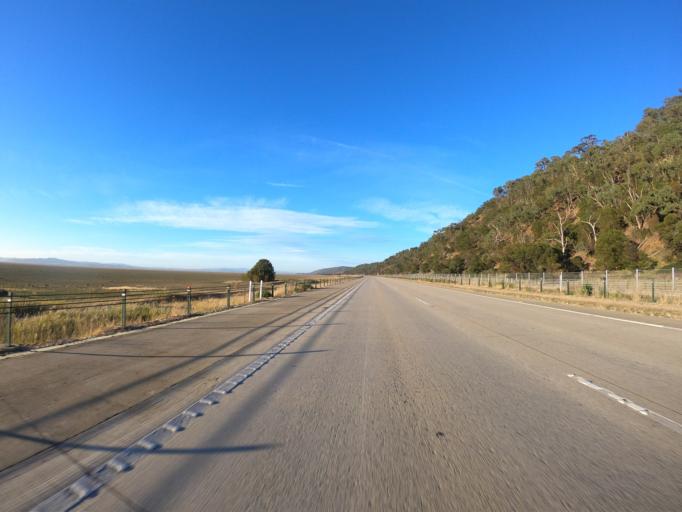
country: AU
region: New South Wales
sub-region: Yass Valley
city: Gundaroo
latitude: -35.0791
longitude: 149.3746
